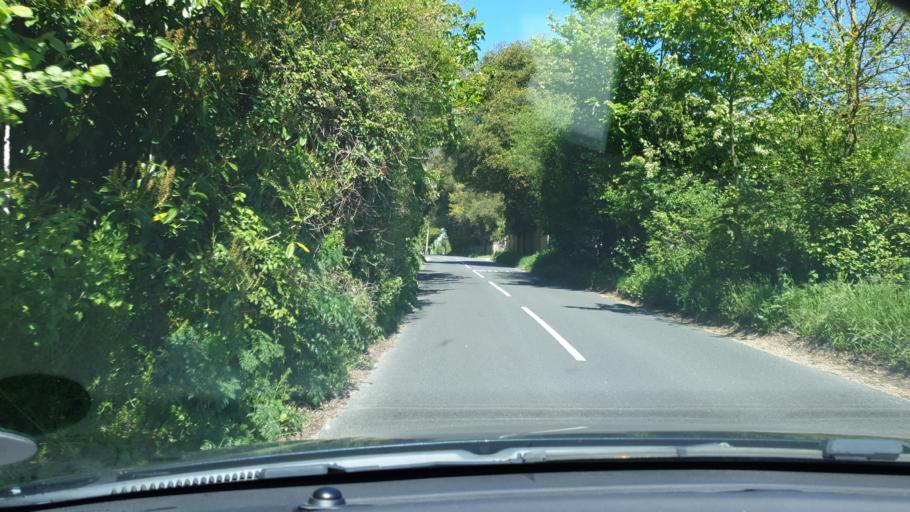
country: GB
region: England
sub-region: Essex
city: Little Clacton
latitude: 51.8688
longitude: 1.1250
